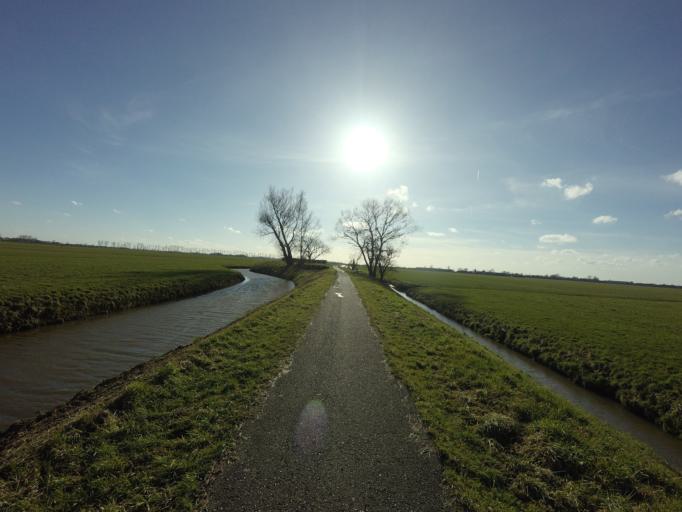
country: NL
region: Utrecht
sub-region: Gemeente Montfoort
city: Montfoort
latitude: 52.0461
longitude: 4.9866
